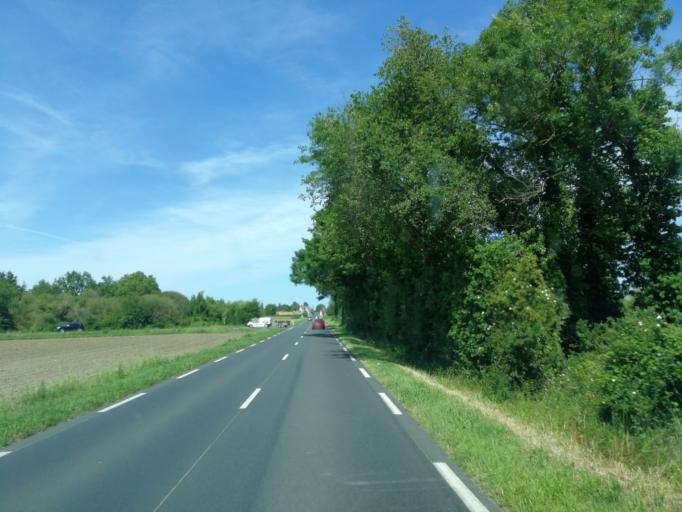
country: FR
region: Poitou-Charentes
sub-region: Departement des Deux-Sevres
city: Saint-Jean-de-Thouars
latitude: 46.9438
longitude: -0.2348
